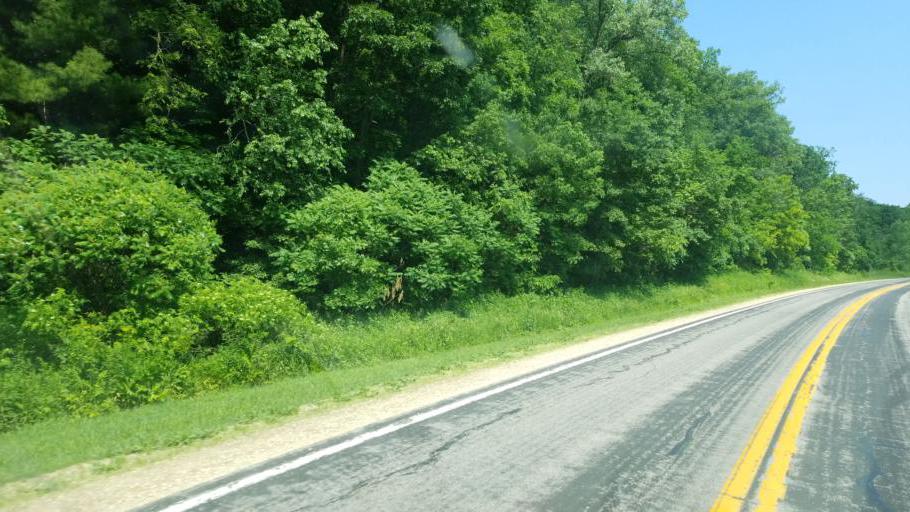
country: US
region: Wisconsin
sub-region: Vernon County
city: Hillsboro
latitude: 43.5928
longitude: -90.5197
